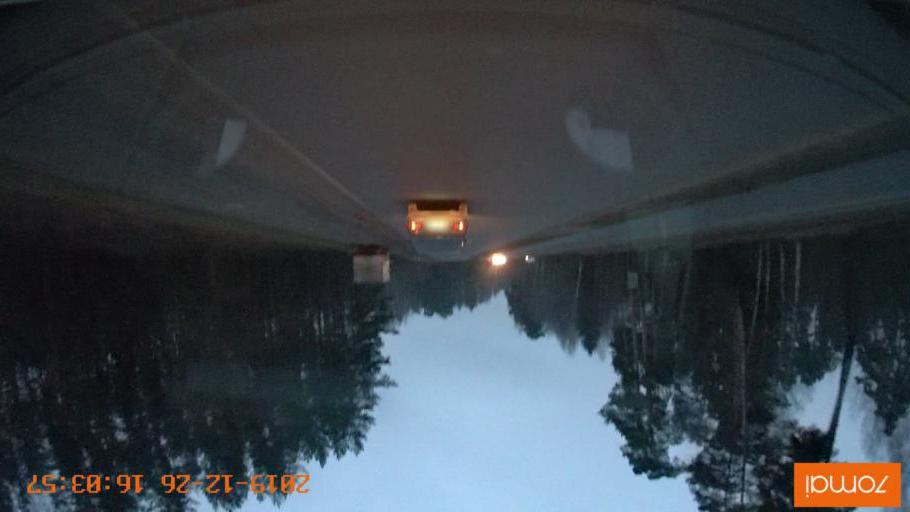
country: RU
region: Jaroslavl
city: Rybinsk
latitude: 58.0096
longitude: 38.8603
